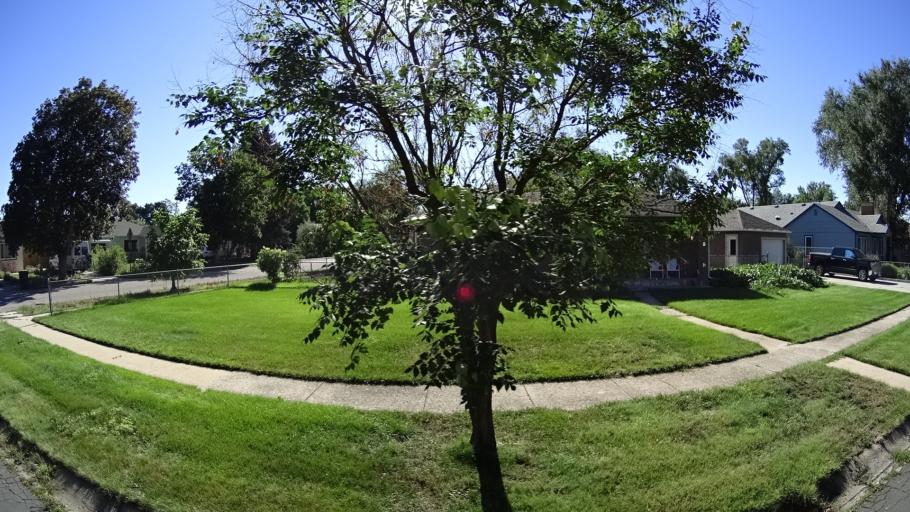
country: US
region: Colorado
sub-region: El Paso County
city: Colorado Springs
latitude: 38.8690
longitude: -104.8146
